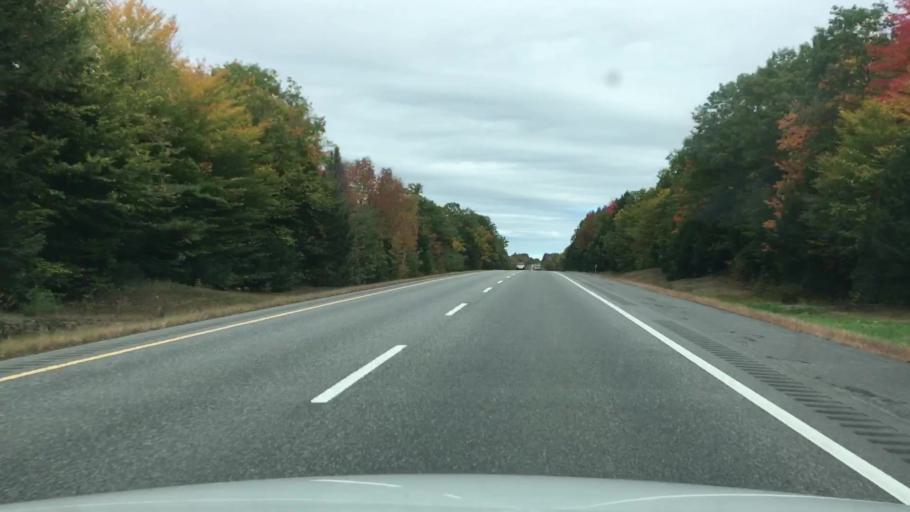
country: US
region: Maine
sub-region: Kennebec County
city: Sidney
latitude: 44.4044
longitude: -69.7503
